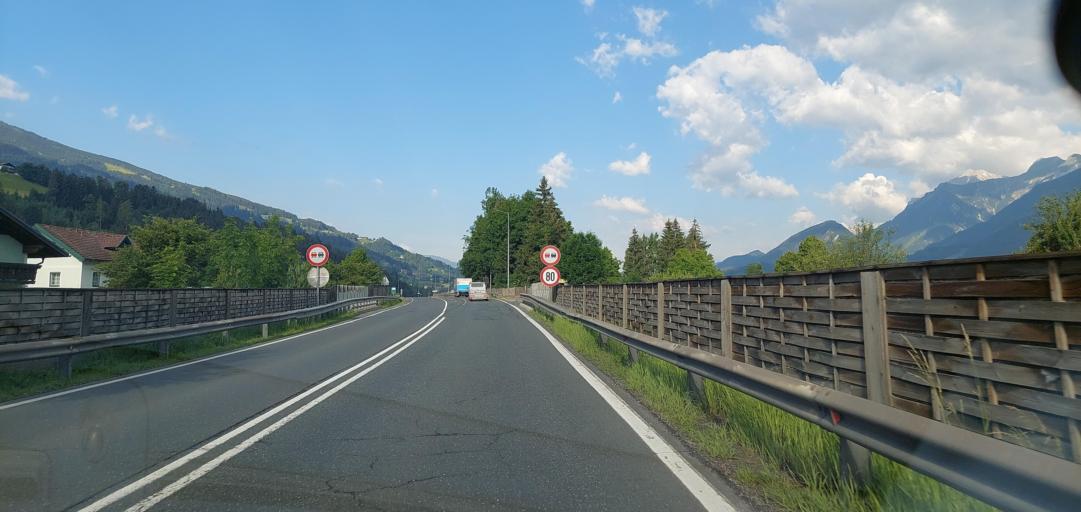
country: AT
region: Styria
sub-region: Politischer Bezirk Liezen
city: Aich
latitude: 47.4179
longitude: 13.8201
